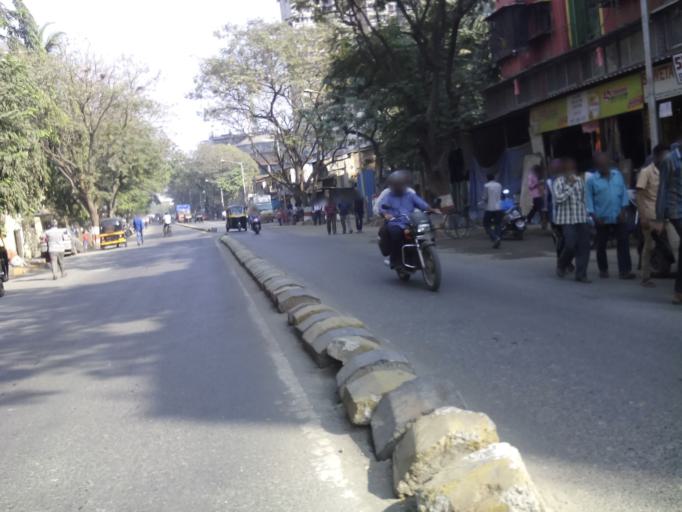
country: IN
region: Maharashtra
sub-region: Mumbai Suburban
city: Borivli
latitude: 19.2072
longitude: 72.8696
